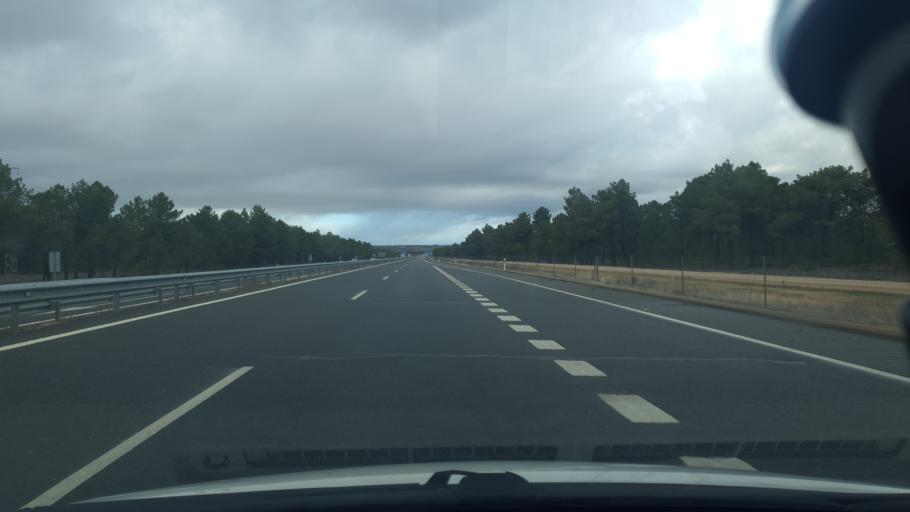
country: ES
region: Castille and Leon
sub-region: Provincia de Segovia
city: Sanchonuno
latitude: 41.3463
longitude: -4.3016
